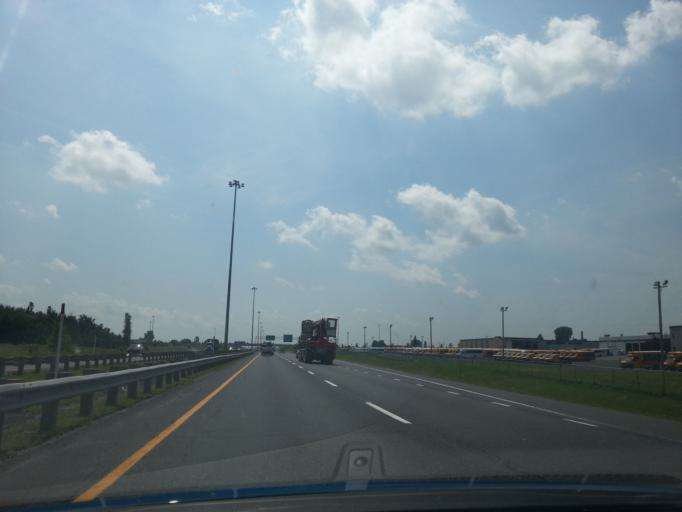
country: CA
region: Quebec
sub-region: Centre-du-Quebec
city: Drummondville
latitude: 45.9060
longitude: -72.5208
